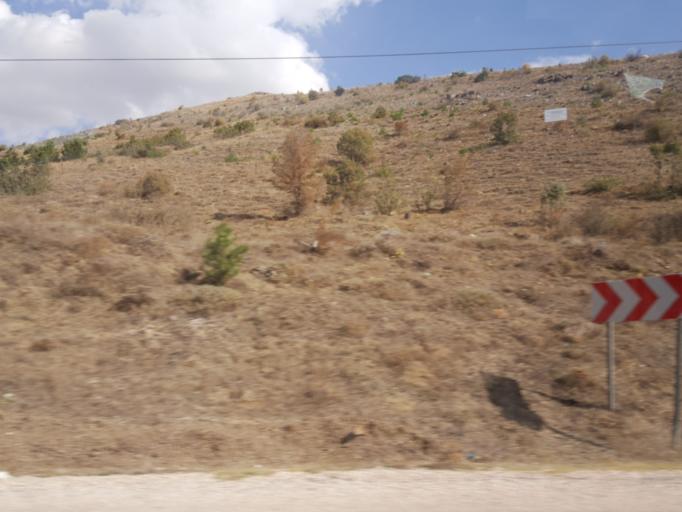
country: TR
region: Tokat
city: Artova
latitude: 40.0988
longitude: 36.3034
